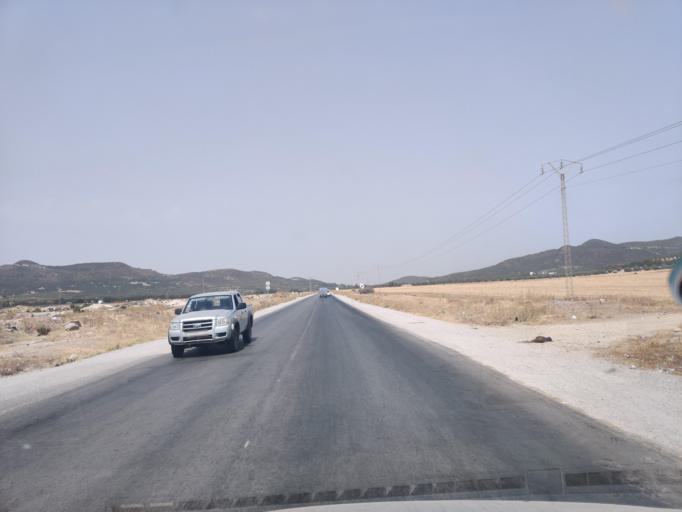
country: TN
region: Tunis
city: Hammam-Lif
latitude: 36.6205
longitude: 10.4099
